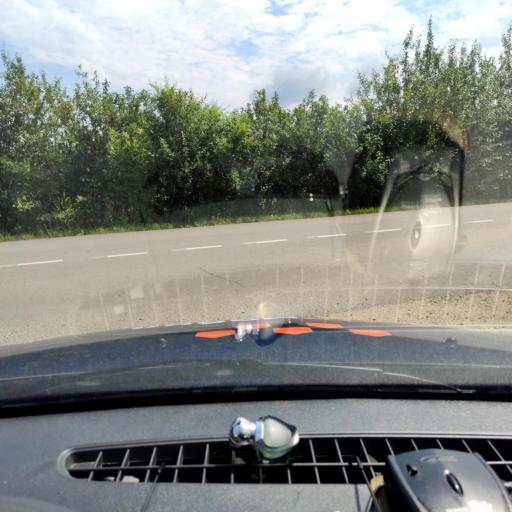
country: RU
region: Voronezj
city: Ramon'
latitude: 52.0713
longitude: 39.3254
